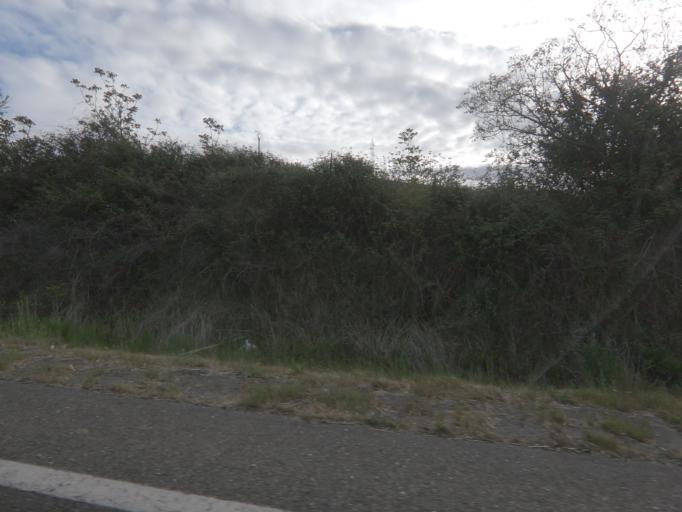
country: ES
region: Extremadura
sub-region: Provincia de Caceres
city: Coria
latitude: 39.9572
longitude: -6.5118
